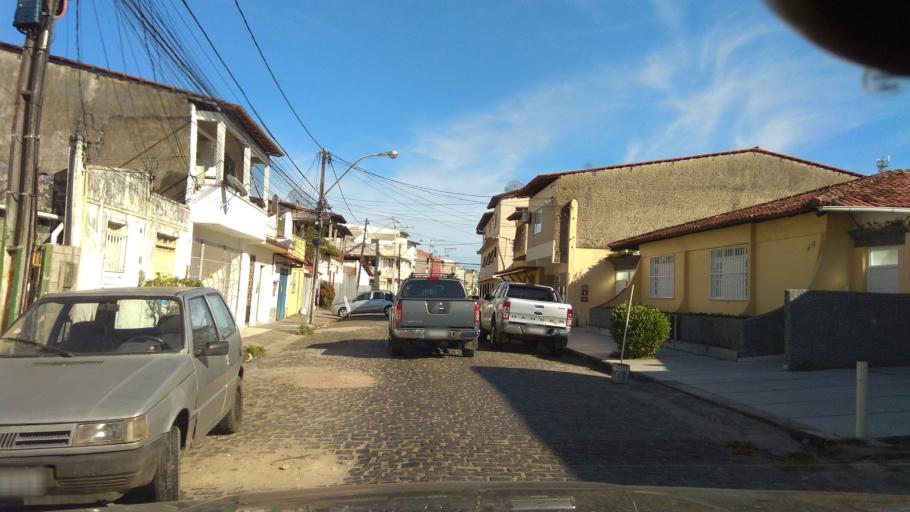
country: BR
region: Bahia
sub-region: Ilheus
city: Ilheus
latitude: -14.8132
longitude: -39.0326
